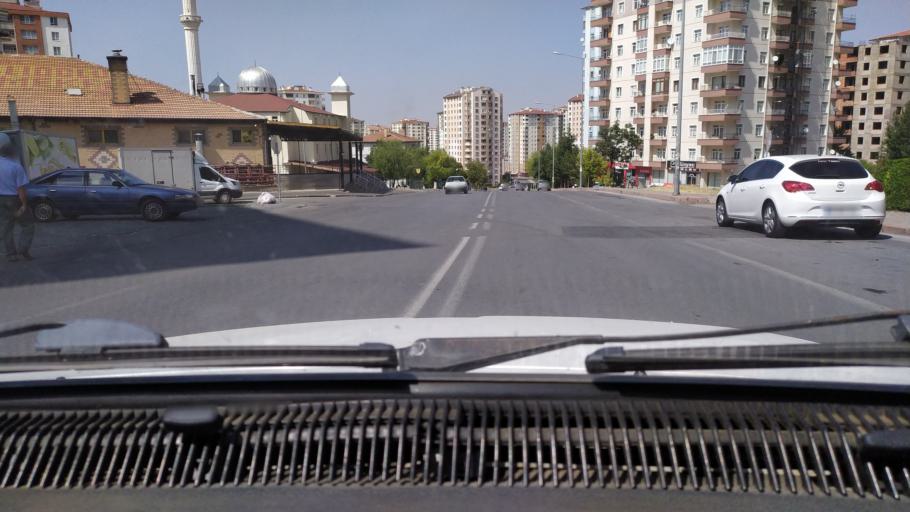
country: TR
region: Kayseri
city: Talas
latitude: 38.7061
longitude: 35.5613
